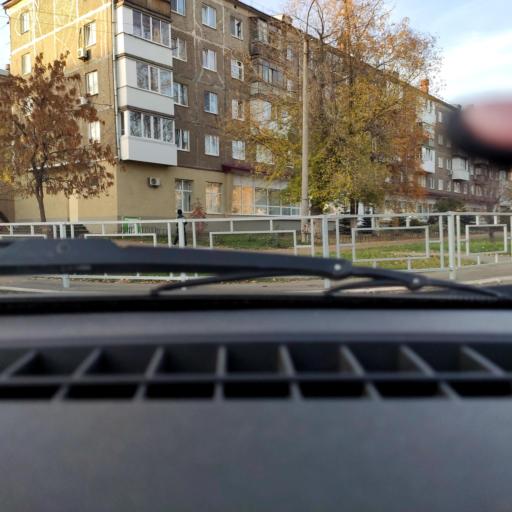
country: RU
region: Bashkortostan
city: Ufa
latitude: 54.8120
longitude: 56.0817
